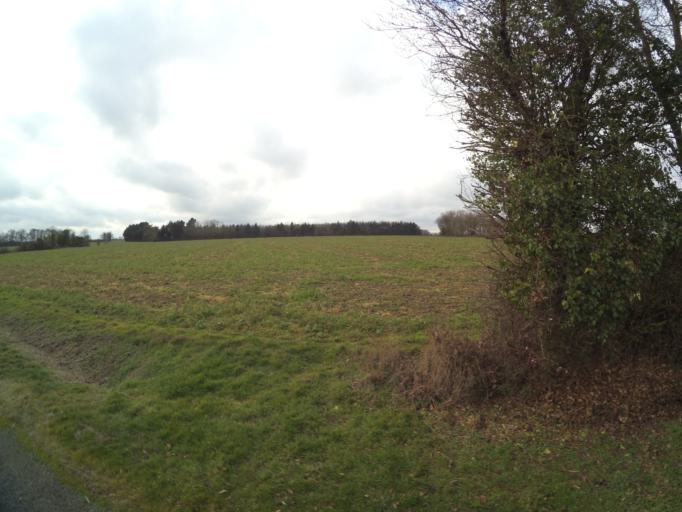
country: FR
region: Pays de la Loire
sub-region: Departement de la Loire-Atlantique
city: Saint-Hilaire-de-Clisson
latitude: 47.0438
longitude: -1.2915
